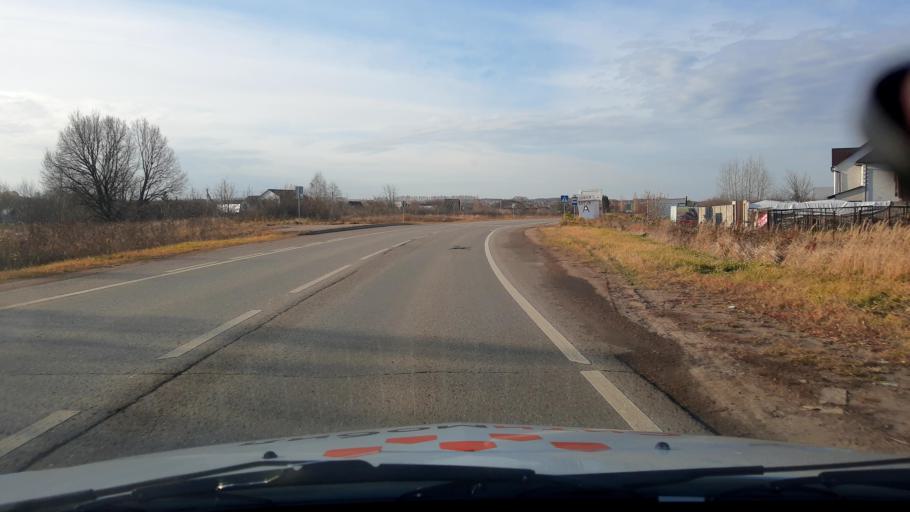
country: RU
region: Bashkortostan
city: Kabakovo
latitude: 54.7255
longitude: 56.1894
